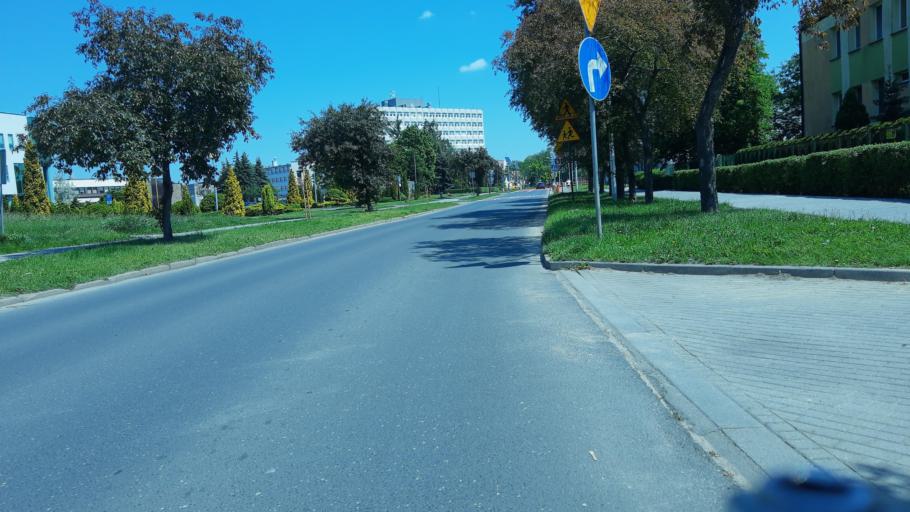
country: PL
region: Lodz Voivodeship
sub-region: Powiat sieradzki
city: Sieradz
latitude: 51.5919
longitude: 18.7299
